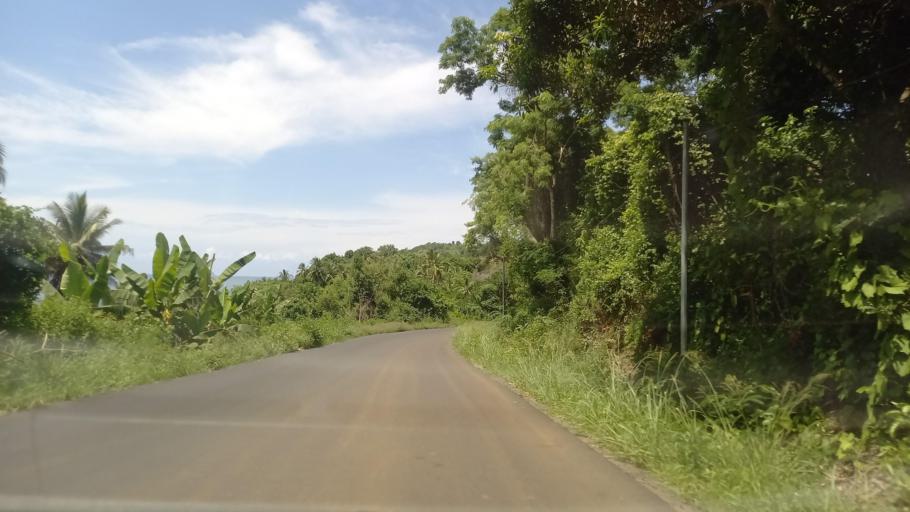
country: YT
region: M'Tsangamouji
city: M'Tsangamouji
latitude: -12.7491
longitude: 45.0613
